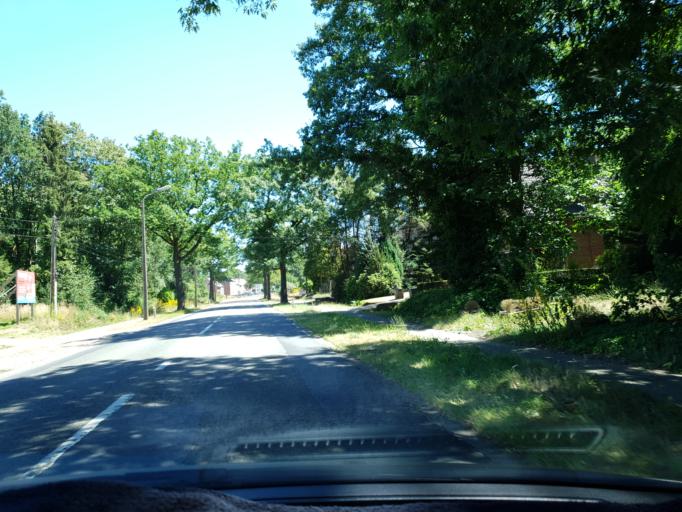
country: BE
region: Flanders
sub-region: Provincie Antwerpen
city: Olen
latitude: 51.1694
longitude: 4.8584
